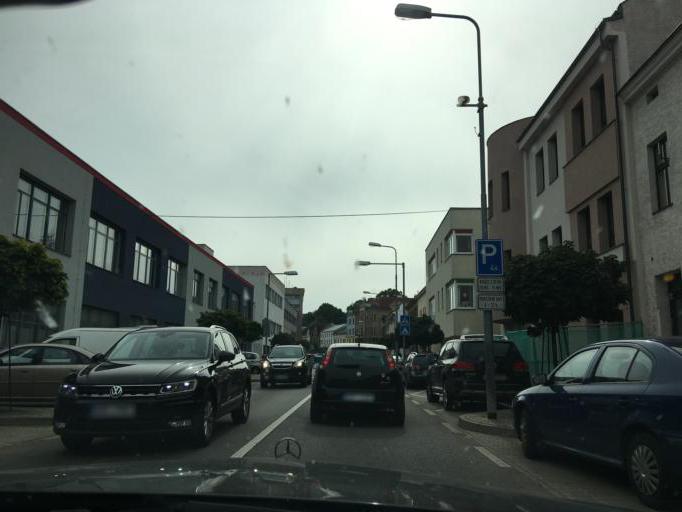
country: CZ
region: Kralovehradecky
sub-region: Okres Nachod
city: Nachod
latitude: 50.4119
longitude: 16.1578
